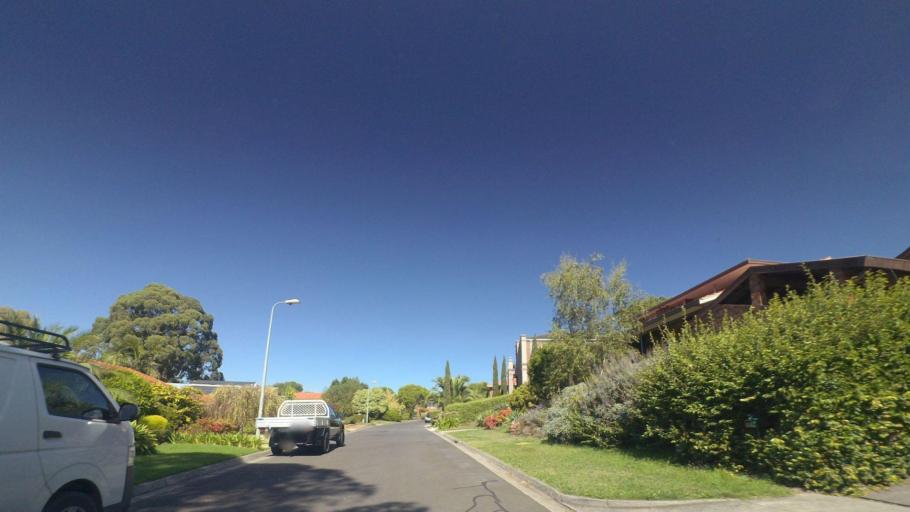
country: AU
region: Victoria
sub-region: Manningham
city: Donvale
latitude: -37.7772
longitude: 145.1692
